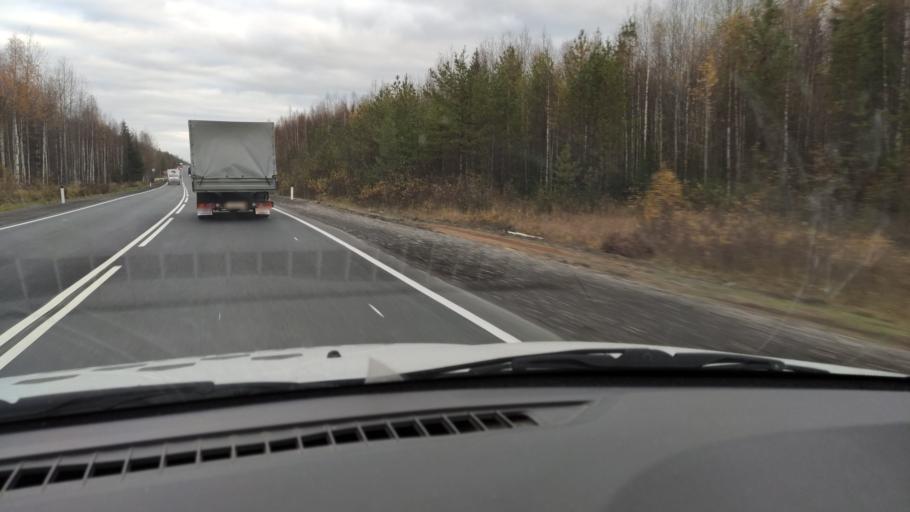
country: RU
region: Kirov
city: Chernaya Kholunitsa
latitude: 58.8747
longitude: 51.4900
